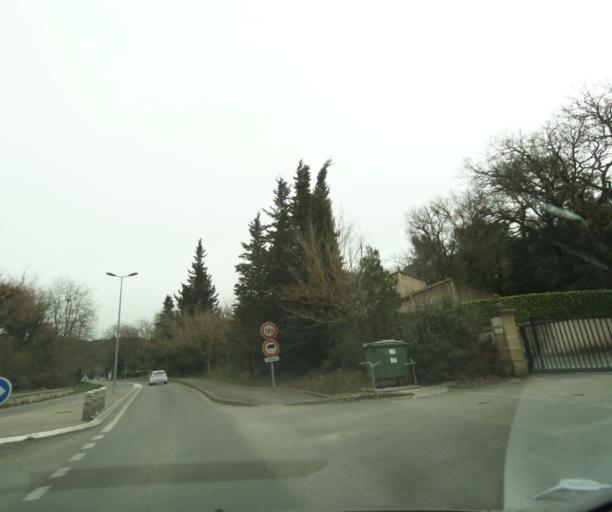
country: FR
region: Provence-Alpes-Cote d'Azur
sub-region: Departement des Bouches-du-Rhone
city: Aix-en-Provence
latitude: 43.5355
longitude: 5.4726
